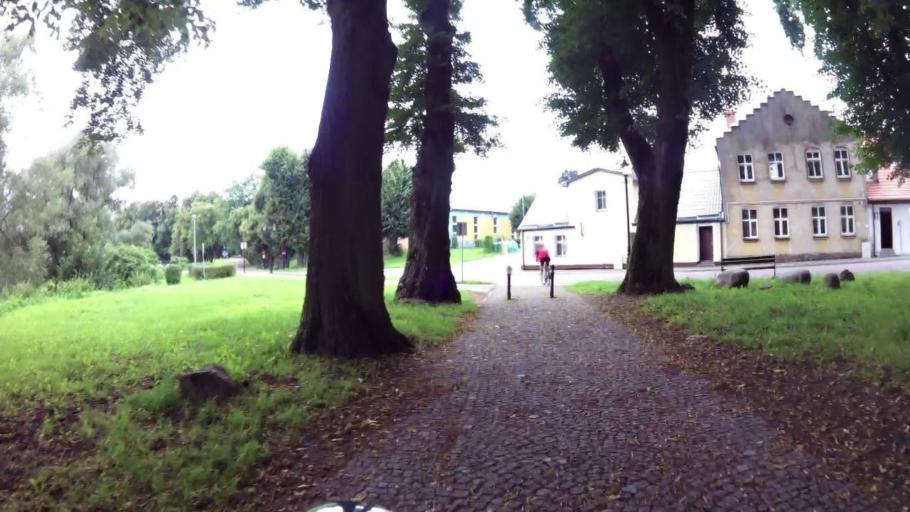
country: PL
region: West Pomeranian Voivodeship
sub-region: Powiat bialogardzki
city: Karlino
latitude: 54.0352
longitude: 15.8756
